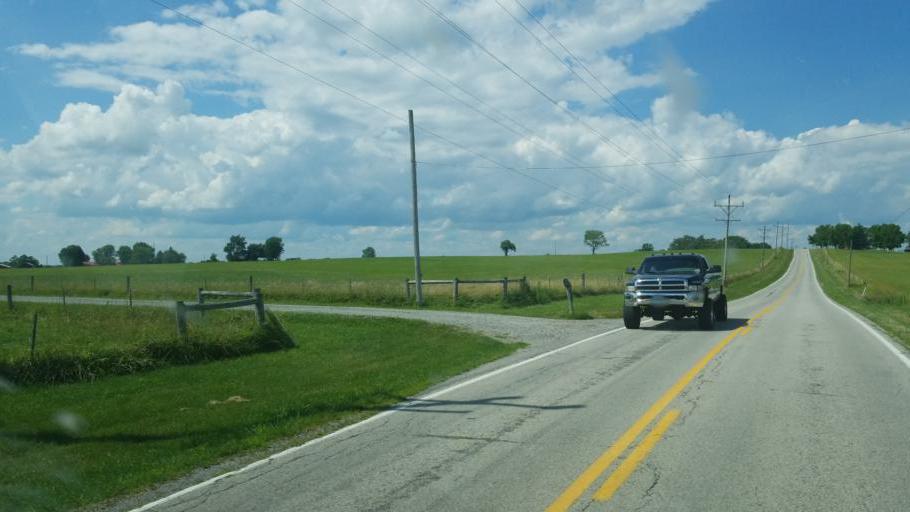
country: US
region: Ohio
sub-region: Highland County
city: Greenfield
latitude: 39.2952
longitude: -83.4096
